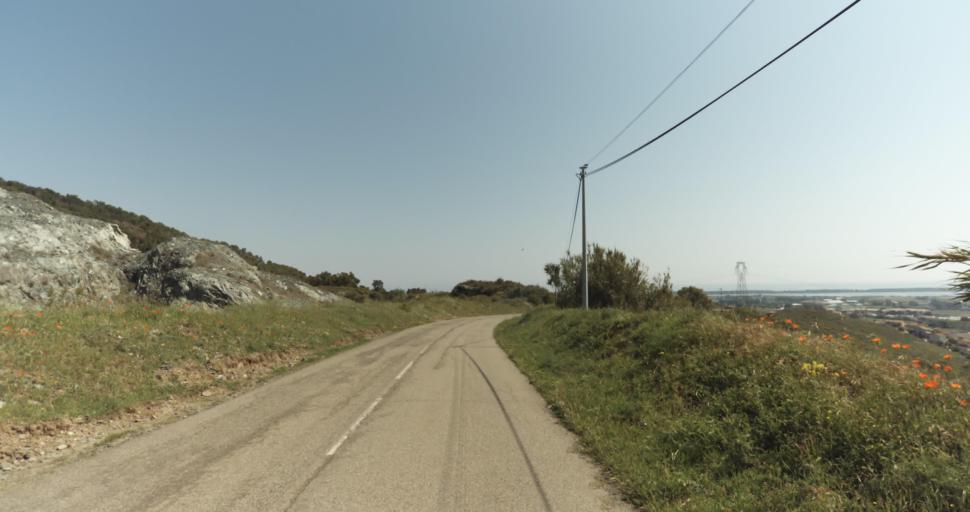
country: FR
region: Corsica
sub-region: Departement de la Haute-Corse
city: Biguglia
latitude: 42.6146
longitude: 9.4210
